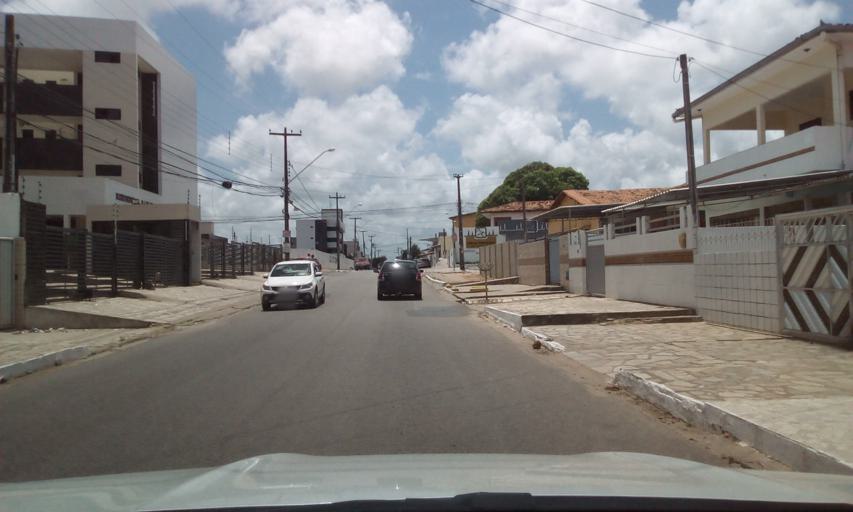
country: BR
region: Paraiba
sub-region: Joao Pessoa
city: Joao Pessoa
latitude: -7.1820
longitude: -34.8659
